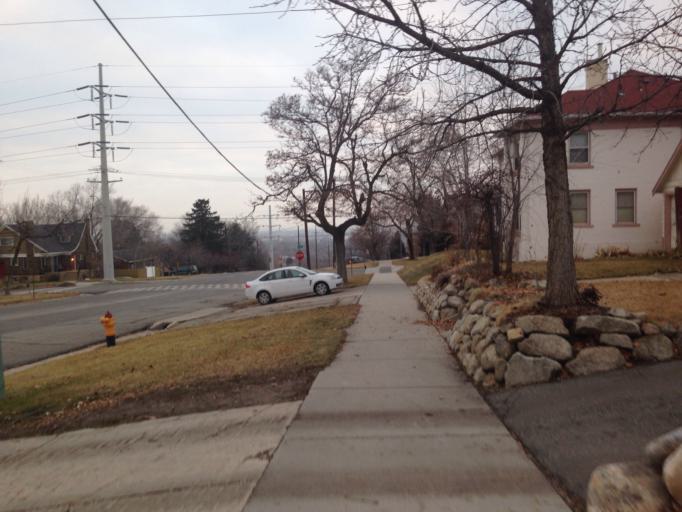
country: US
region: Utah
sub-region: Salt Lake County
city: Salt Lake City
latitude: 40.7543
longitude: -111.8586
